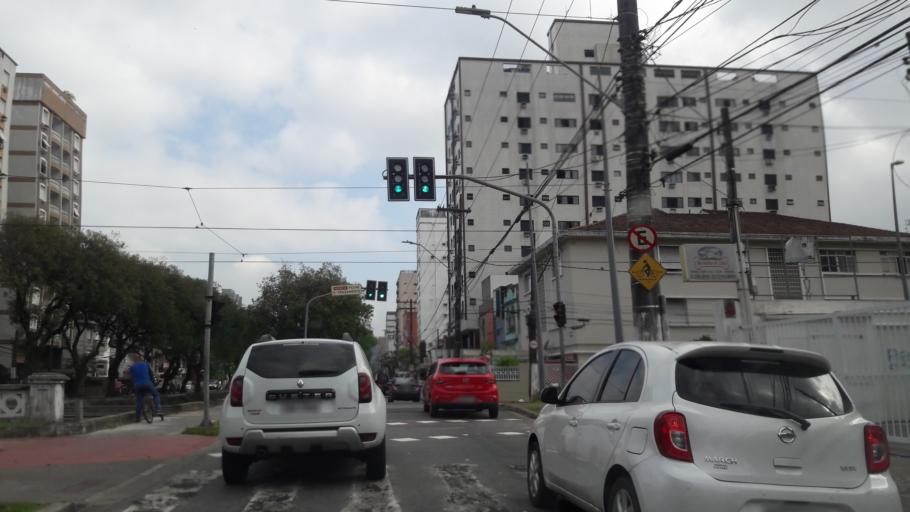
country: BR
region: Sao Paulo
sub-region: Santos
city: Santos
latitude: -23.9633
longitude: -46.3453
